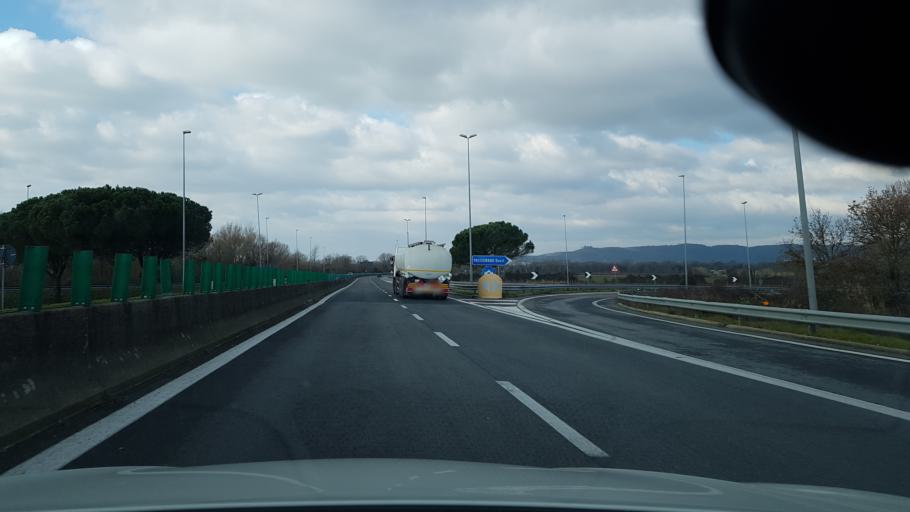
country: IT
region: Umbria
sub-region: Provincia di Perugia
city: Passignano sul Trasimeno
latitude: 43.1956
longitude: 12.1078
